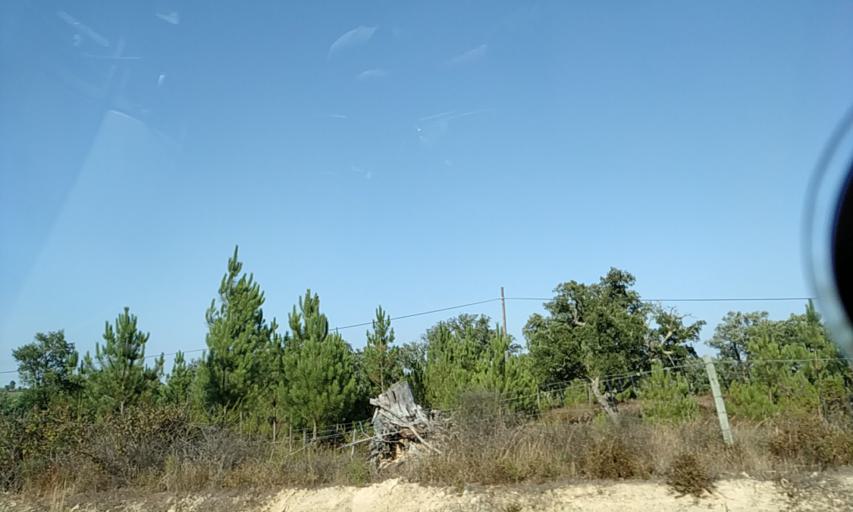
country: PT
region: Santarem
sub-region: Almeirim
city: Fazendas de Almeirim
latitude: 39.0771
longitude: -8.5667
